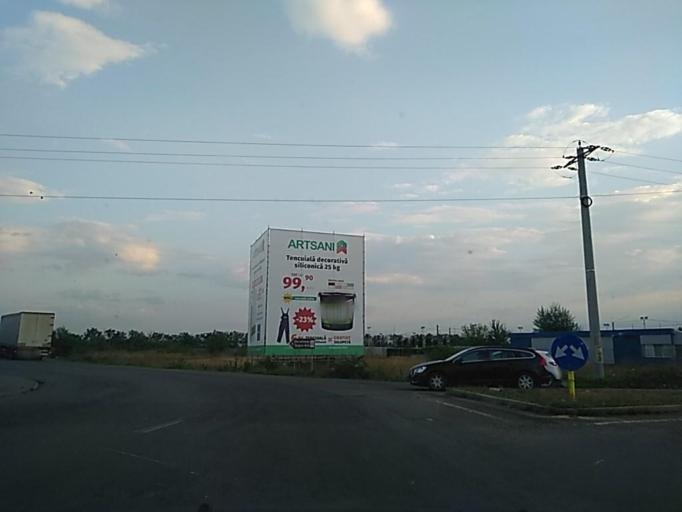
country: RO
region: Prahova
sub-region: Comuna Targsoru Vechi
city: Strejnicu
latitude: 44.9244
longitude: 25.9811
